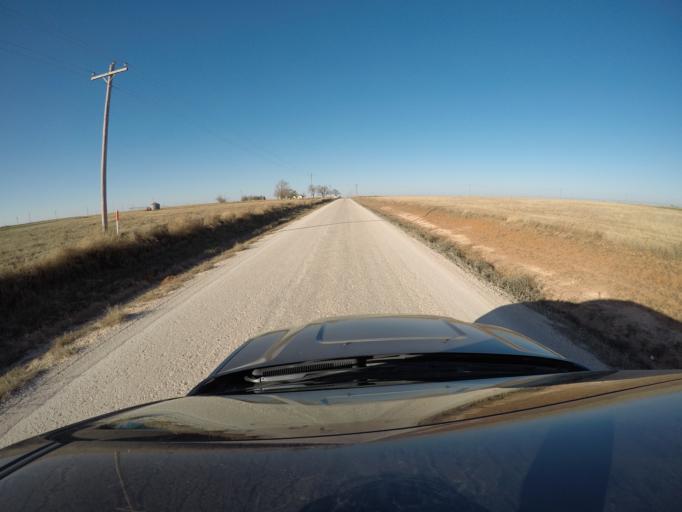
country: US
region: New Mexico
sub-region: Curry County
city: Texico
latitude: 34.3445
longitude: -103.1083
